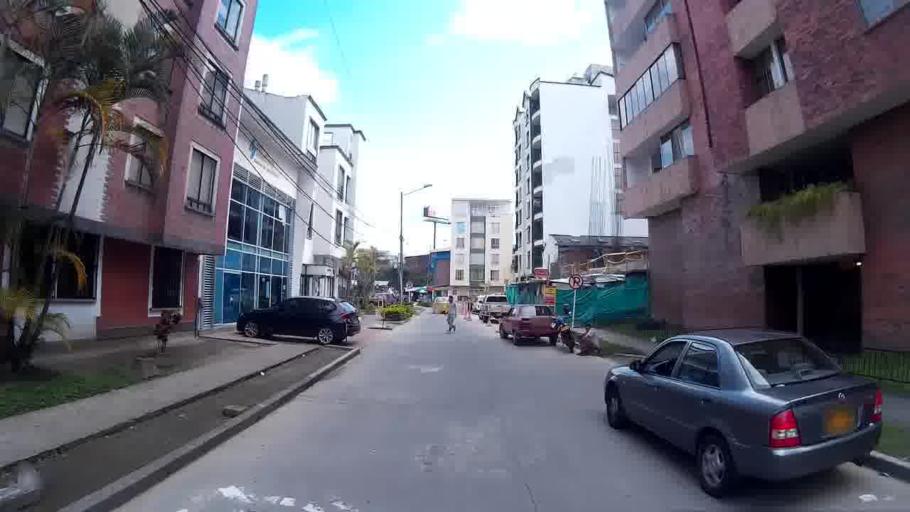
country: CO
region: Quindio
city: Armenia
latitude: 4.5448
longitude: -75.6617
